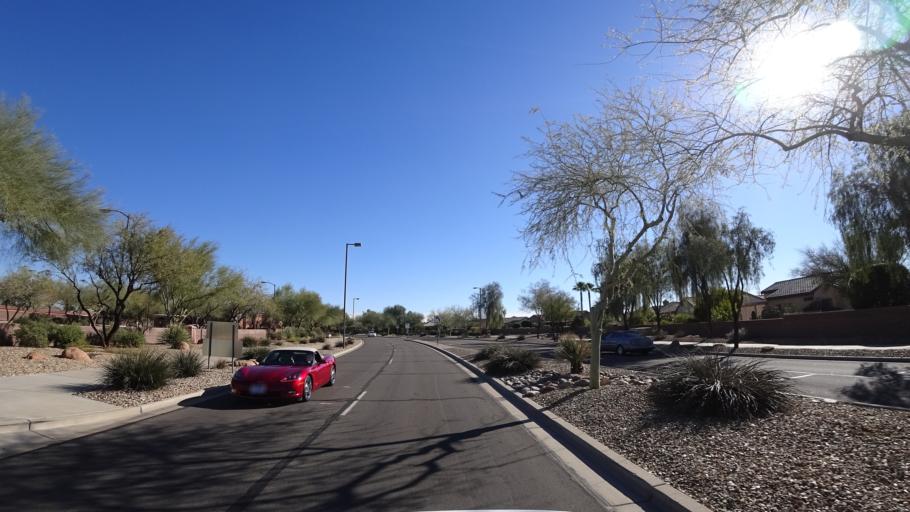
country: US
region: Arizona
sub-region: Maricopa County
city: Sun City West
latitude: 33.6595
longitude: -112.3866
